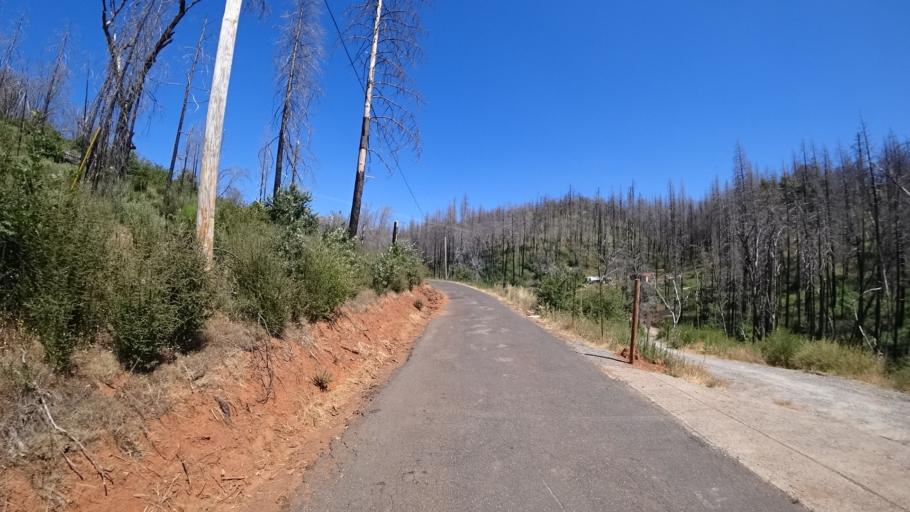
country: US
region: California
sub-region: Calaveras County
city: Mountain Ranch
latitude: 38.2832
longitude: -120.5664
